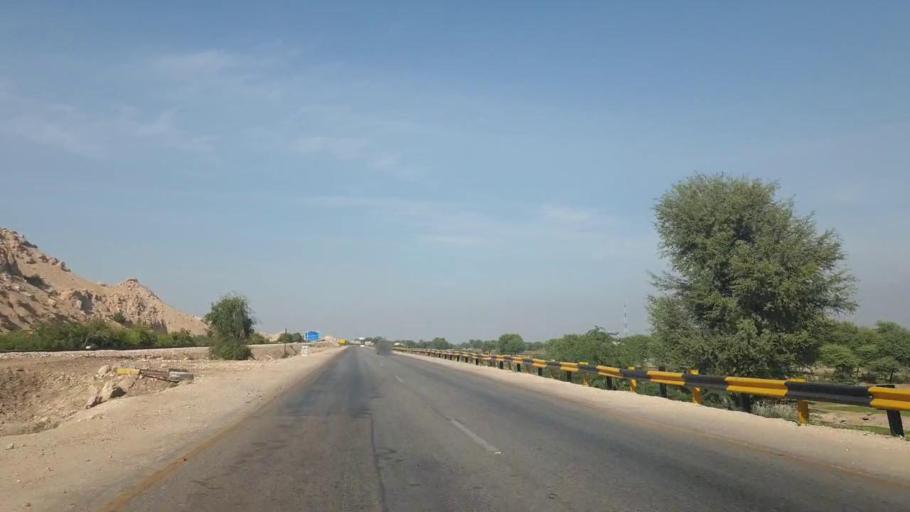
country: PK
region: Sindh
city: Sehwan
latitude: 26.2926
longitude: 67.8943
